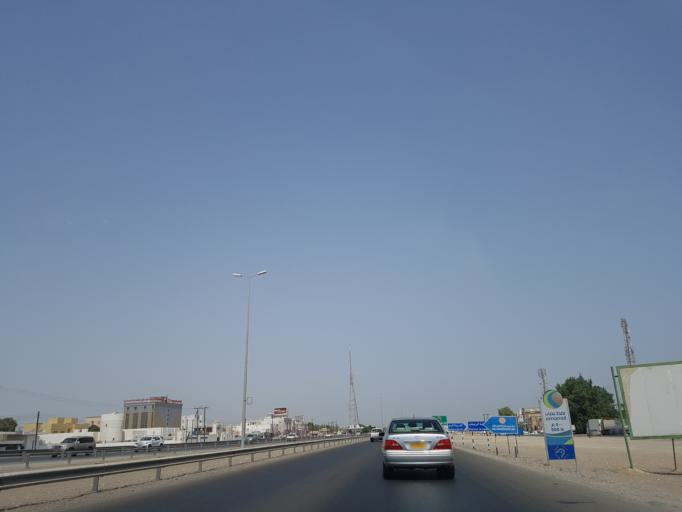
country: OM
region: Al Batinah
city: Saham
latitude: 24.1394
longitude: 56.8794
